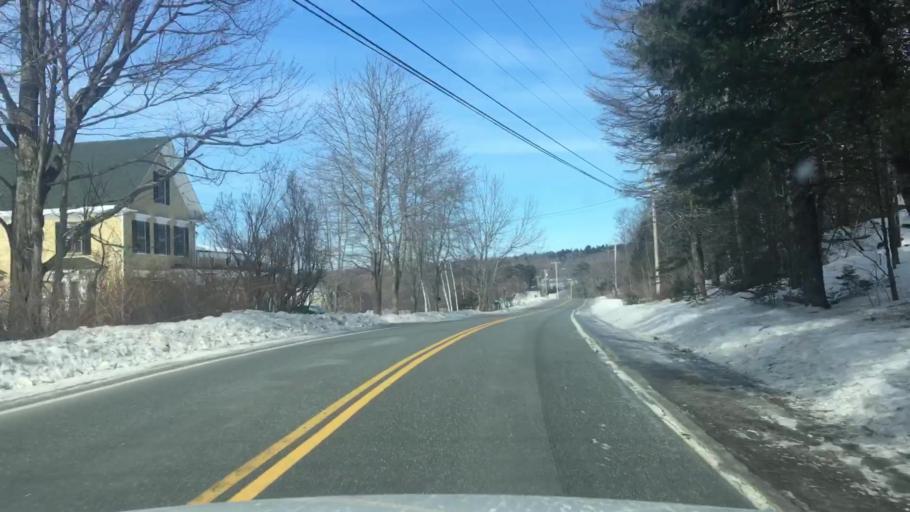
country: US
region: Maine
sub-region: Hancock County
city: Orland
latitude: 44.5476
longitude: -68.7427
